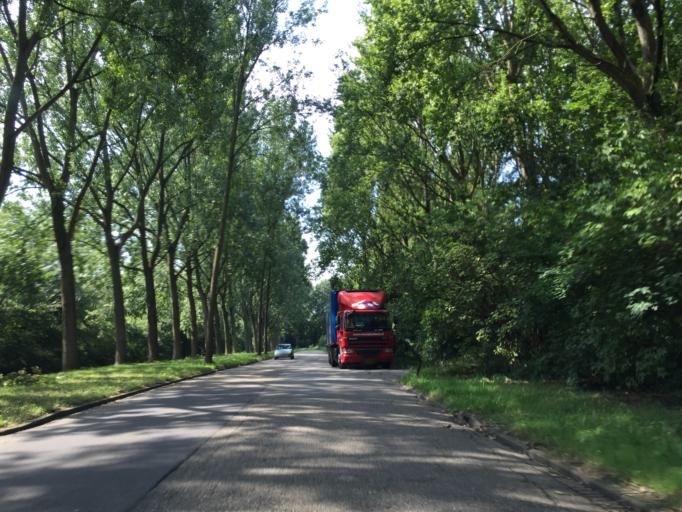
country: NL
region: South Holland
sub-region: Gemeente Rotterdam
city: Rotterdam
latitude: 51.9515
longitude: 4.4522
